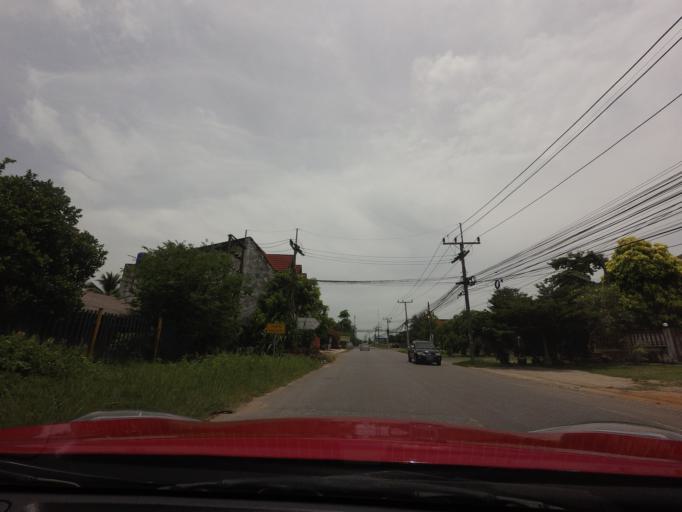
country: TH
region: Songkhla
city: Hat Yai
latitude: 7.0015
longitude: 100.5259
